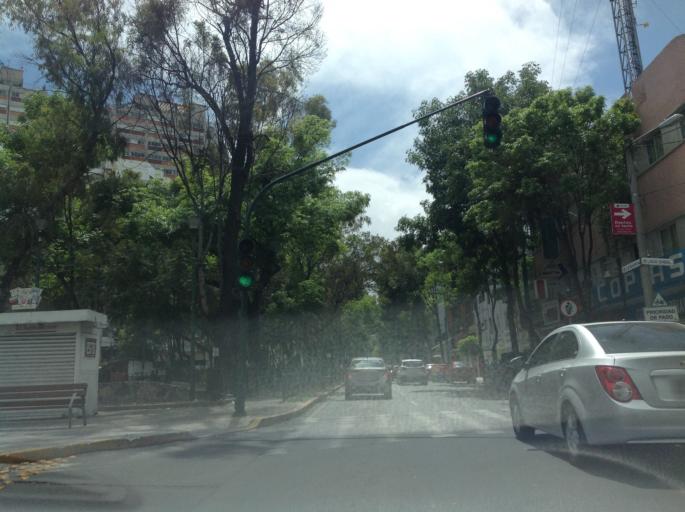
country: MX
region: Mexico City
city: Miguel Hidalgo
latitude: 19.4560
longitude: -99.1948
